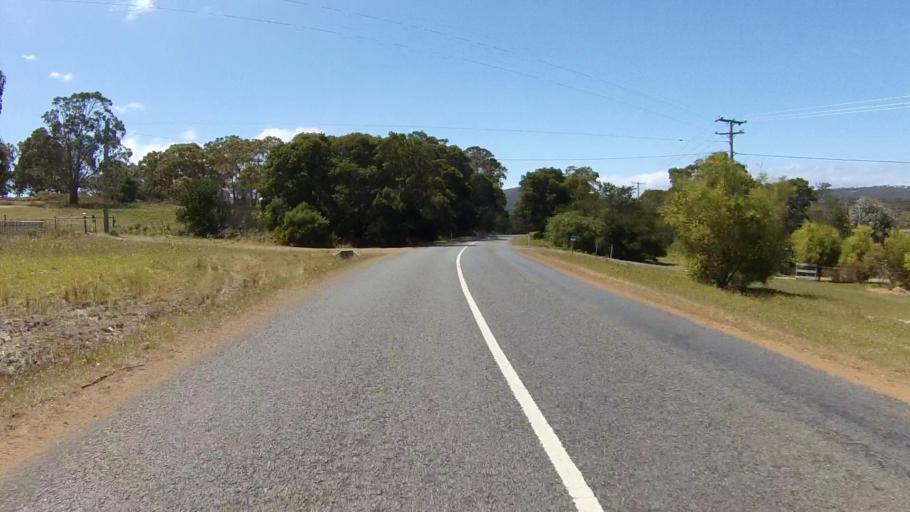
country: AU
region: Tasmania
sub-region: Clarence
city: Sandford
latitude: -42.9937
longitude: 147.4770
